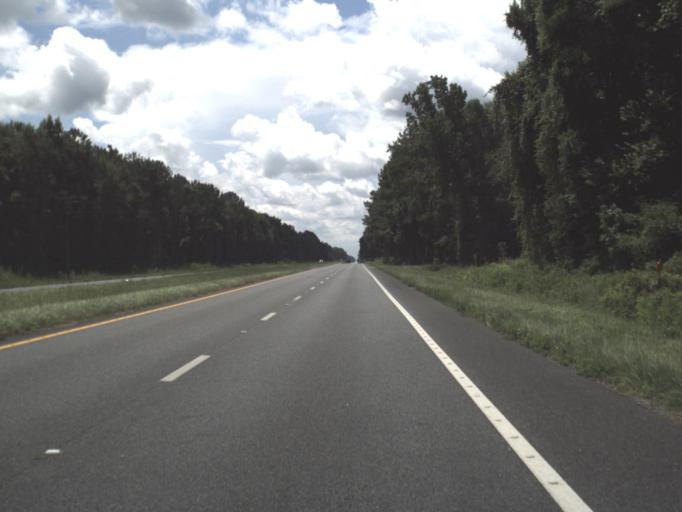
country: US
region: Florida
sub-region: Taylor County
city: Perry
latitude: 30.2998
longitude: -83.7451
